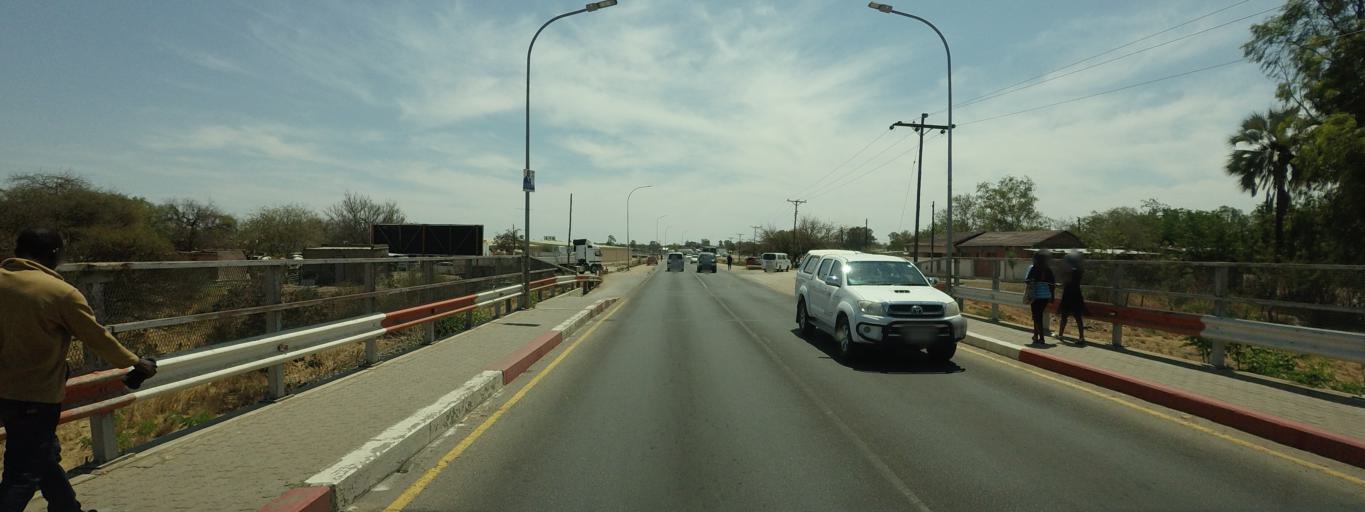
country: BW
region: North East
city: Francistown
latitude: -21.1707
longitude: 27.4995
